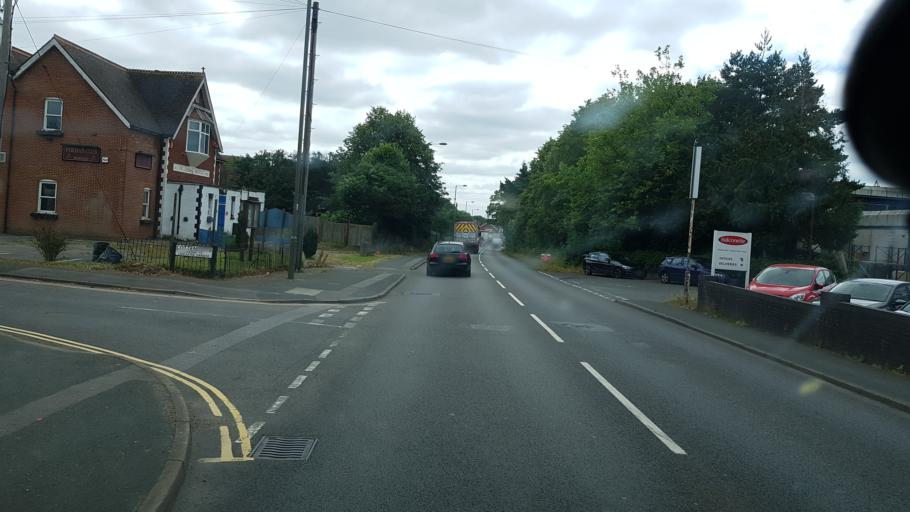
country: GB
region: England
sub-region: Surrey
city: Lingfield
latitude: 51.1943
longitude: -0.0516
